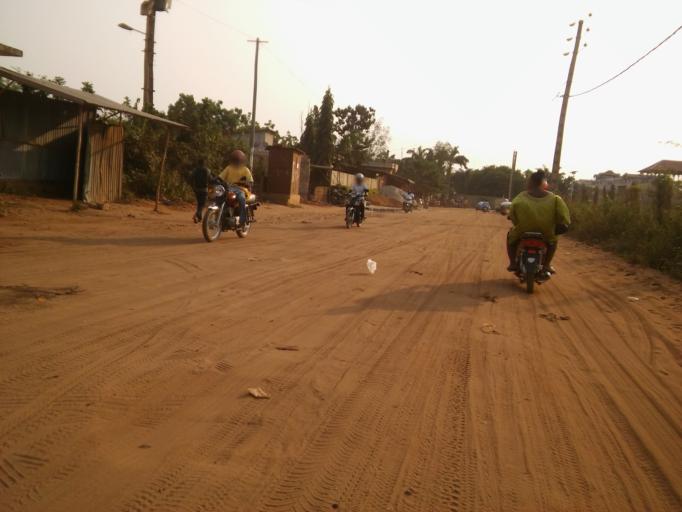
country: BJ
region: Atlantique
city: Abomey-Calavi
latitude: 6.4151
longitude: 2.3327
